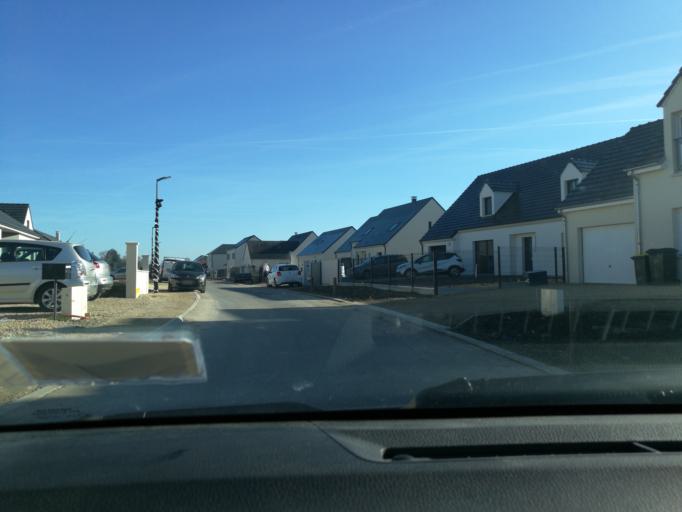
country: FR
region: Centre
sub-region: Departement du Loiret
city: Chaingy
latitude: 47.8819
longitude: 1.7793
